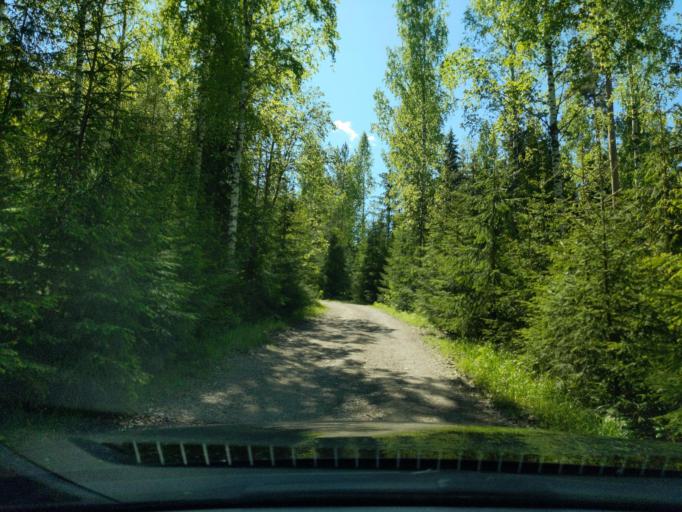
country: FI
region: Paijanne Tavastia
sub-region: Lahti
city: Lahti
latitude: 61.0535
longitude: 25.6959
